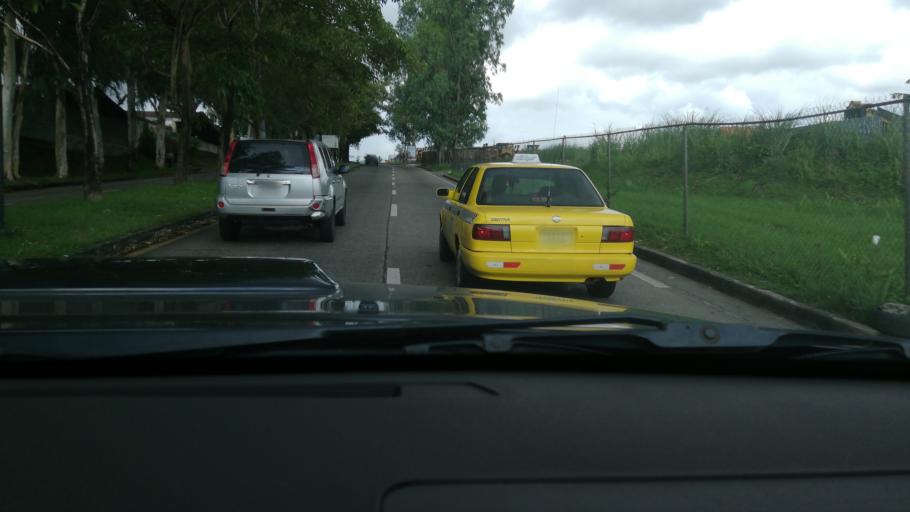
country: PA
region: Panama
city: San Miguelito
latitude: 9.0418
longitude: -79.4803
